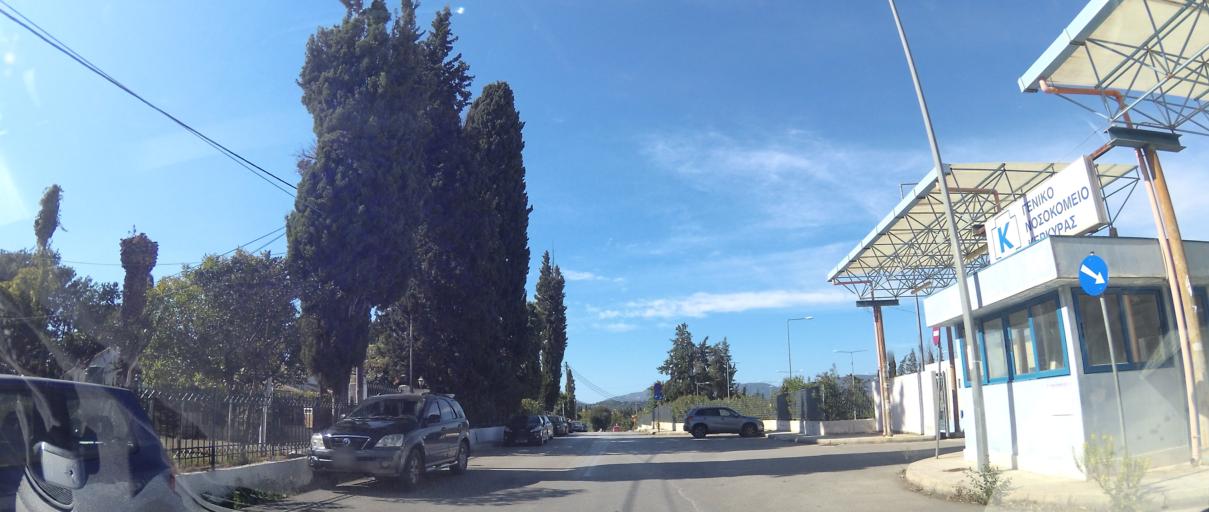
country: GR
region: Ionian Islands
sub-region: Nomos Kerkyras
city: Kontokali
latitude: 39.6428
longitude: 19.8502
